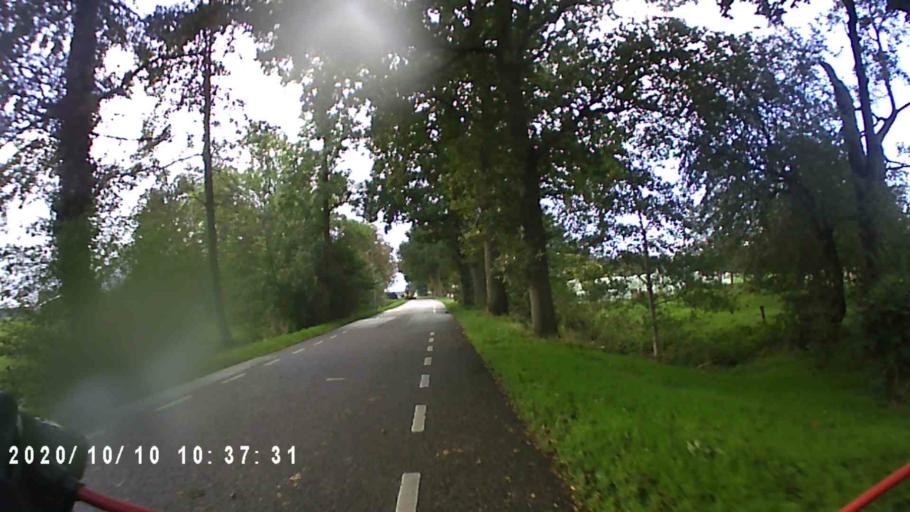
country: NL
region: Groningen
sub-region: Gemeente Grootegast
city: Grootegast
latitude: 53.1835
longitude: 6.2997
